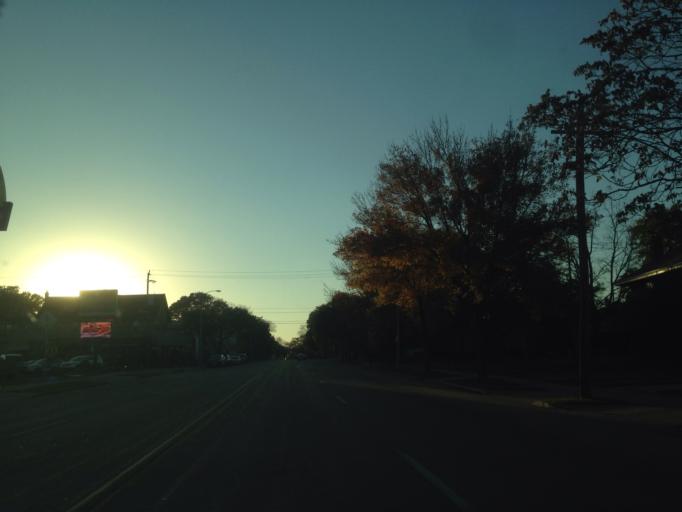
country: US
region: Wisconsin
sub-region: Milwaukee County
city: Wauwatosa
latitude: 43.0362
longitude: -87.9924
